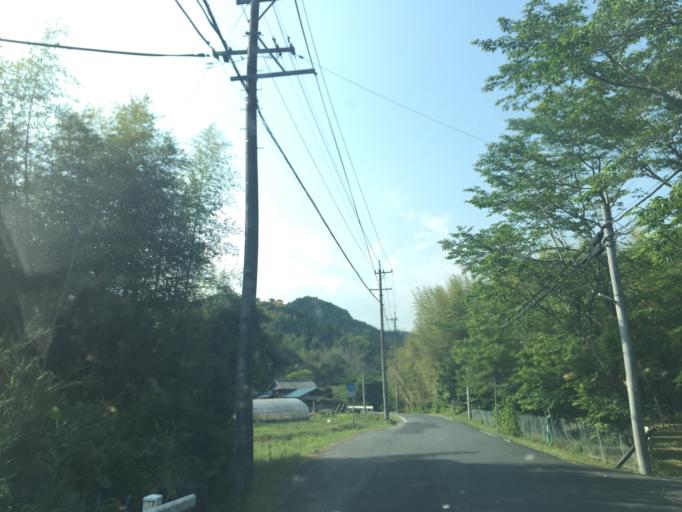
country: JP
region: Shizuoka
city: Kakegawa
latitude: 34.8269
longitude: 138.0431
